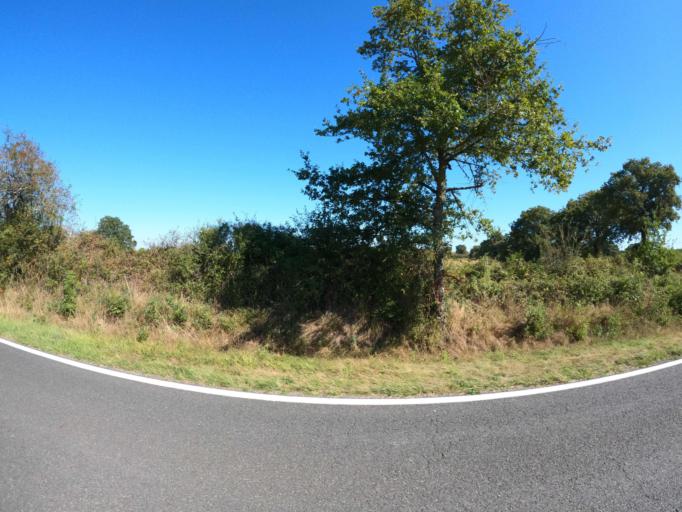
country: FR
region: Poitou-Charentes
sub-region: Departement de la Vienne
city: Lathus-Saint-Remy
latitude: 46.3041
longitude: 0.9880
